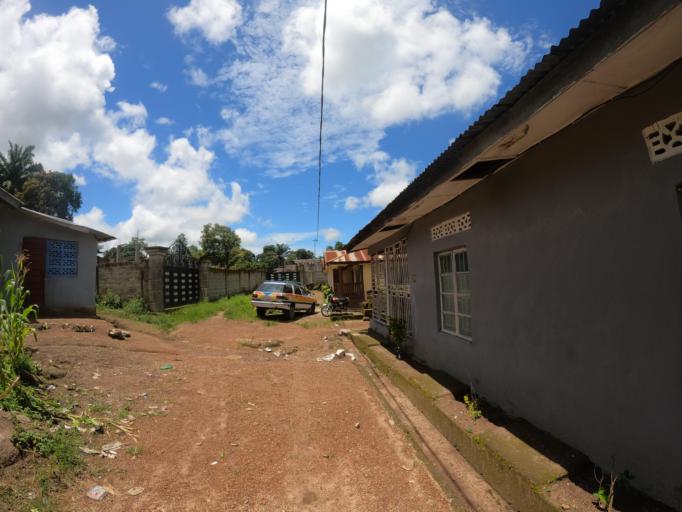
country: SL
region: Northern Province
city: Makeni
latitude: 8.8941
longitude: -12.0622
